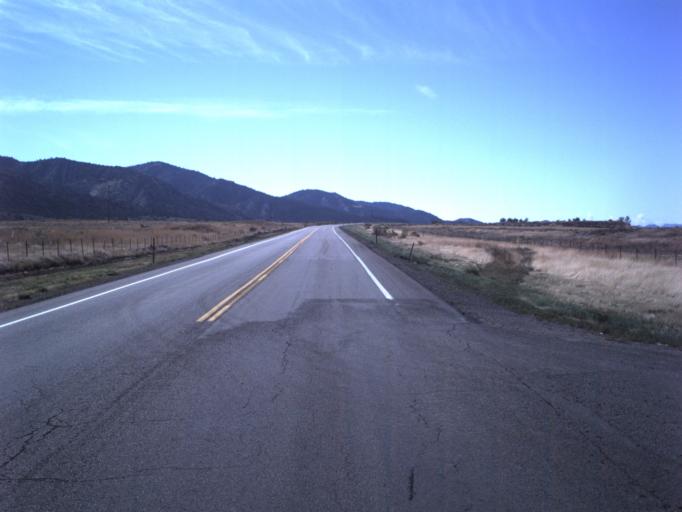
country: US
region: Utah
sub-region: Juab County
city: Nephi
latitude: 39.5181
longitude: -111.8680
